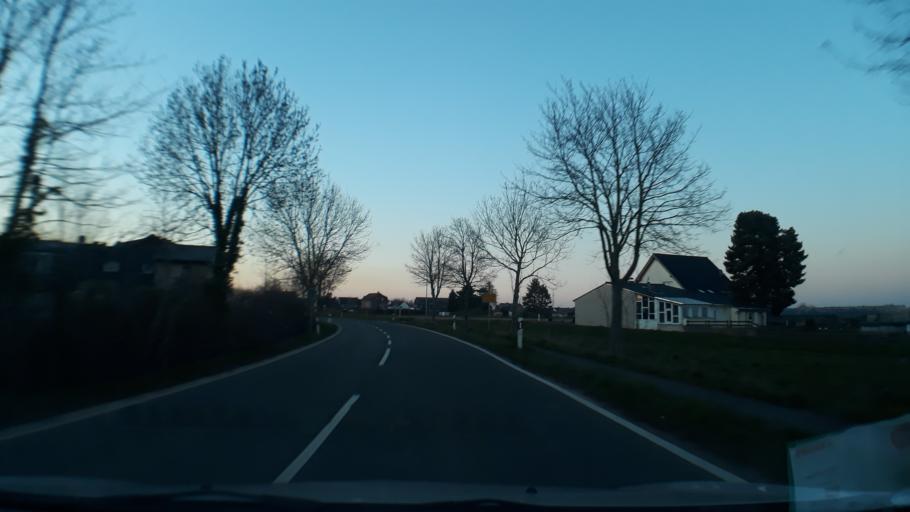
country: DE
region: North Rhine-Westphalia
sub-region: Regierungsbezirk Koln
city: Norvenich
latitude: 50.8104
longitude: 6.5891
